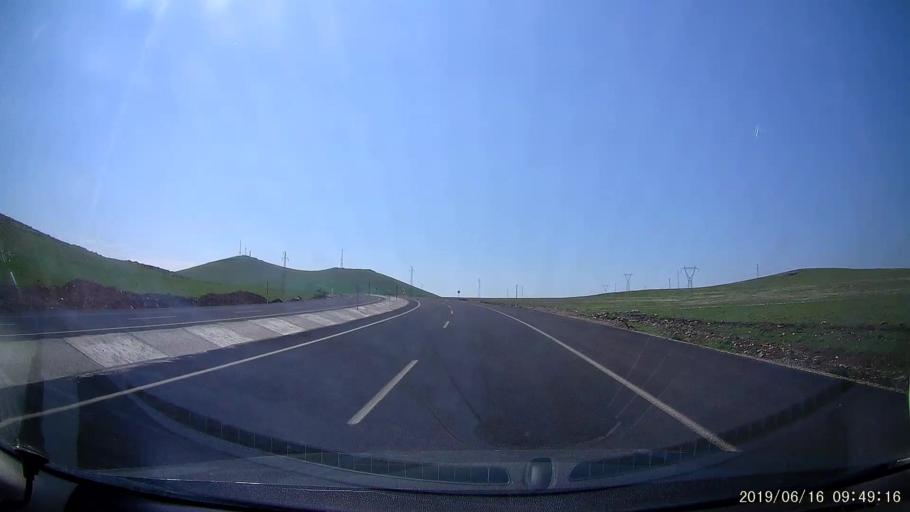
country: TR
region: Kars
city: Digor
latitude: 40.4232
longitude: 43.3570
